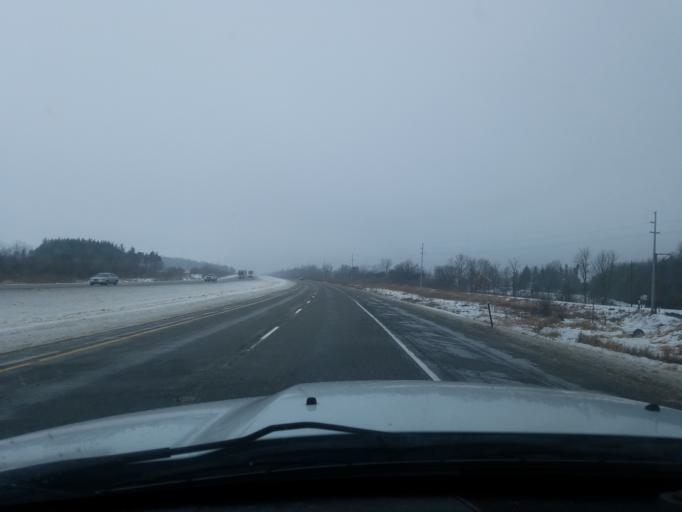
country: US
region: Indiana
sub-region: Fulton County
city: Rochester
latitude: 41.0121
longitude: -86.1690
